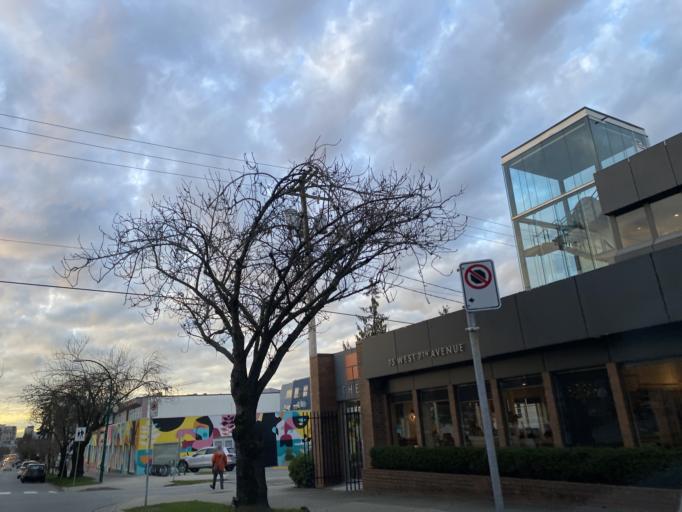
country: CA
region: British Columbia
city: Vancouver
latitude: 49.2647
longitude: -123.1064
